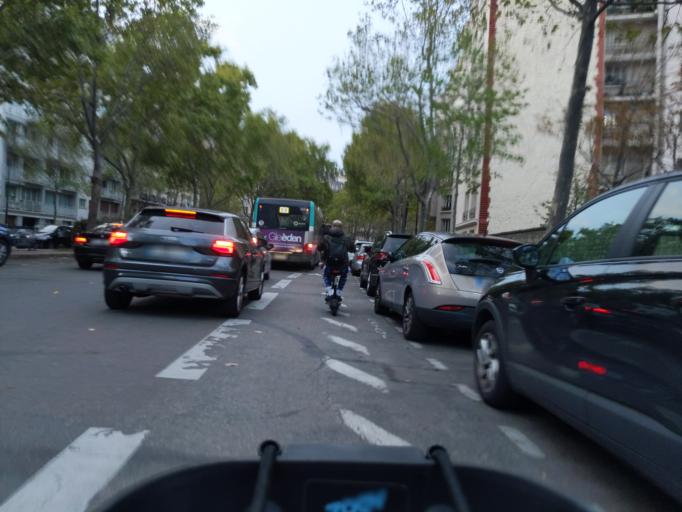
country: FR
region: Ile-de-France
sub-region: Departement des Hauts-de-Seine
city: Boulogne-Billancourt
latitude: 48.8444
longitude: 2.2590
